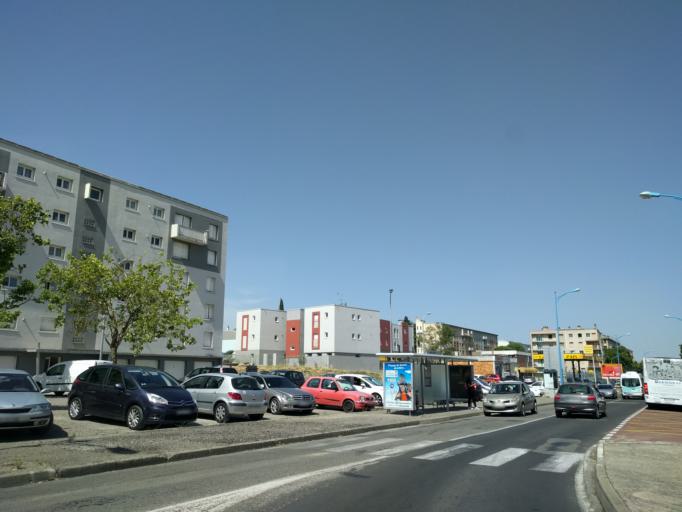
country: FR
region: Languedoc-Roussillon
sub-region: Departement de l'Aude
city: Carcassonne
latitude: 43.2130
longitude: 2.3713
